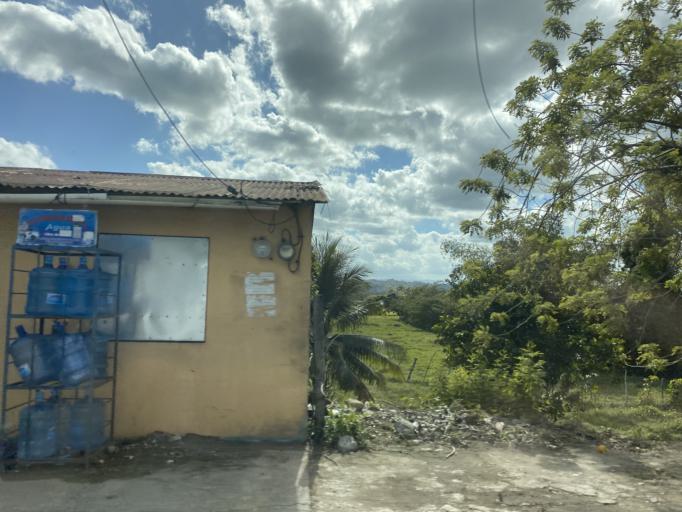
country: DO
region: Espaillat
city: Jamao al Norte
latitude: 19.6713
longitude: -70.3720
